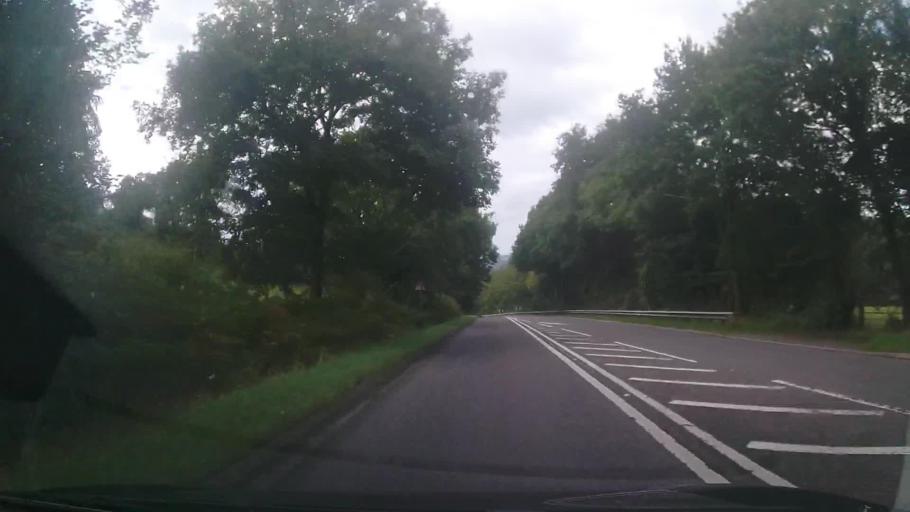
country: GB
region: Wales
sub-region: Gwynedd
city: Dolgellau
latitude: 52.7494
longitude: -3.8471
